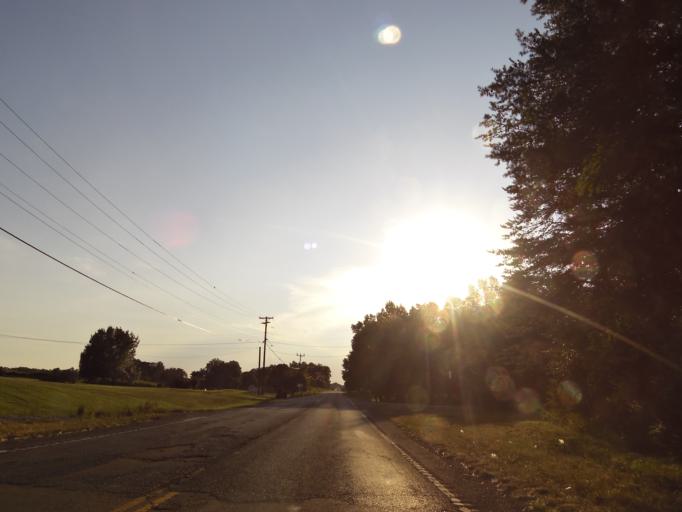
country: US
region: Tennessee
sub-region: McMinn County
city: Englewood
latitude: 35.4258
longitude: -84.5188
